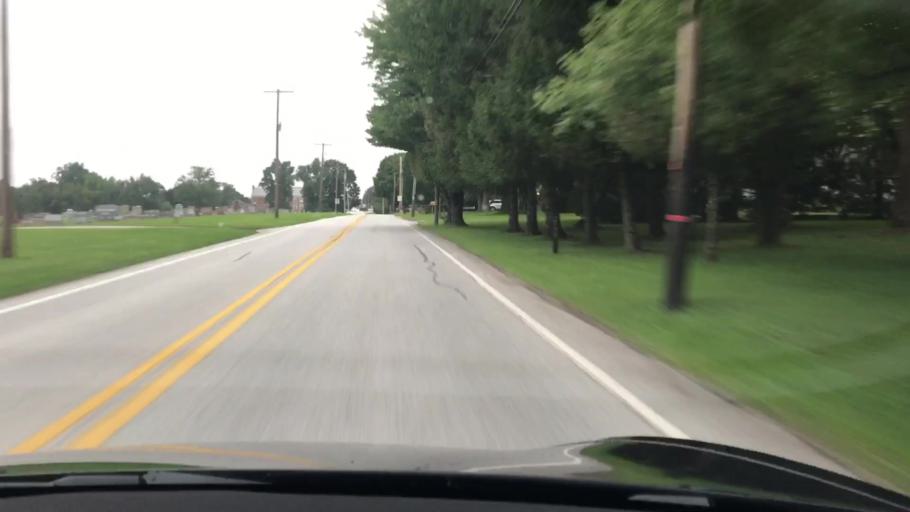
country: US
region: Pennsylvania
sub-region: York County
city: Dover
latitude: 39.9876
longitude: -76.8623
